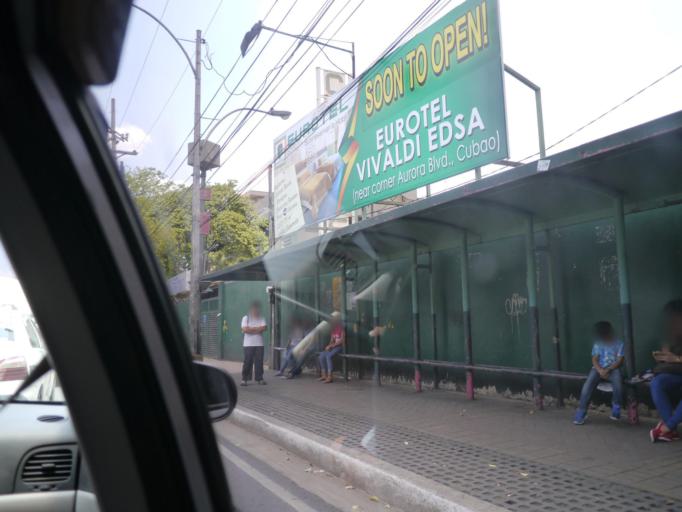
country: PH
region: Metro Manila
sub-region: Quezon City
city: Quezon City
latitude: 14.6386
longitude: 121.0466
